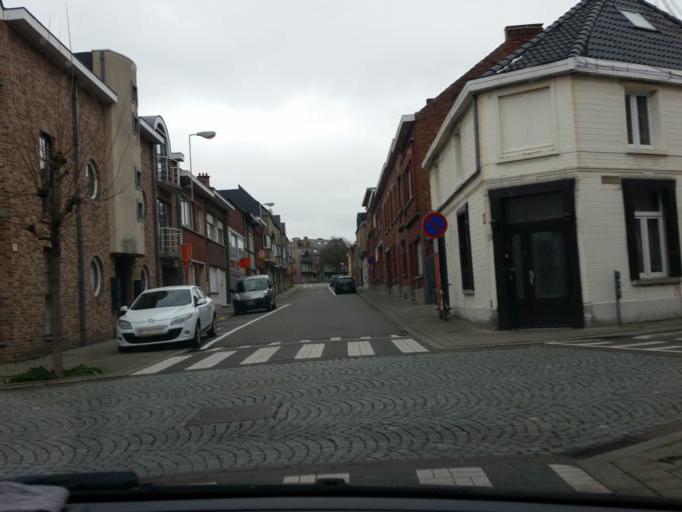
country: BE
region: Flanders
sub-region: Provincie Vlaams-Brabant
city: Machelen
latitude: 50.9097
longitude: 4.4350
